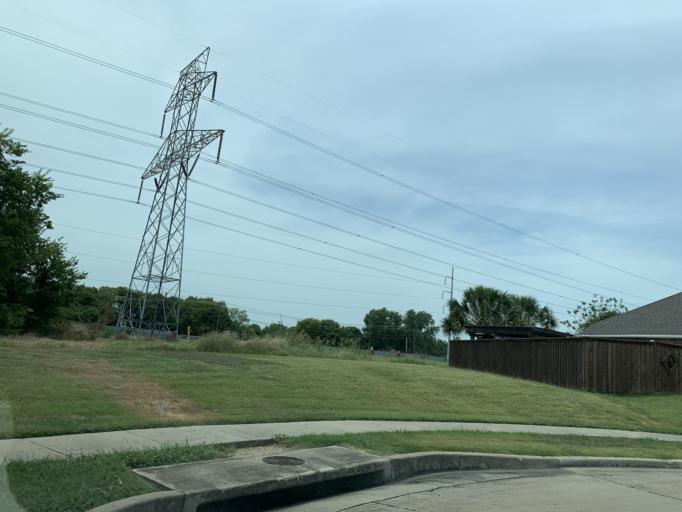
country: US
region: Texas
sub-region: Dallas County
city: Grand Prairie
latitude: 32.6595
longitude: -97.0193
